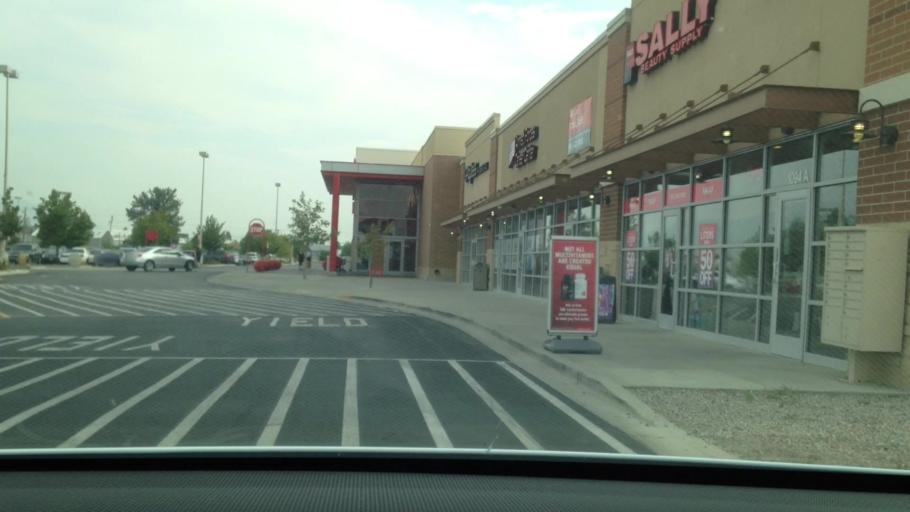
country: US
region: Utah
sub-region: Salt Lake County
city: Salt Lake City
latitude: 40.7456
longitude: -111.9016
